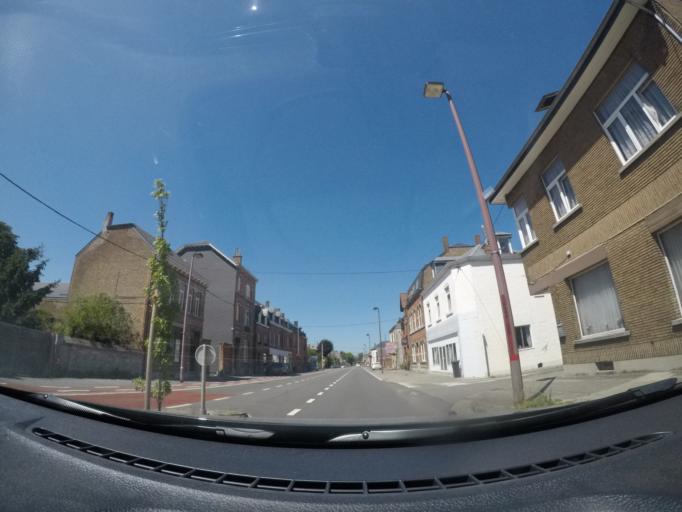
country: BE
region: Wallonia
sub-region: Province de Namur
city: Beauraing
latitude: 50.1132
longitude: 4.9554
